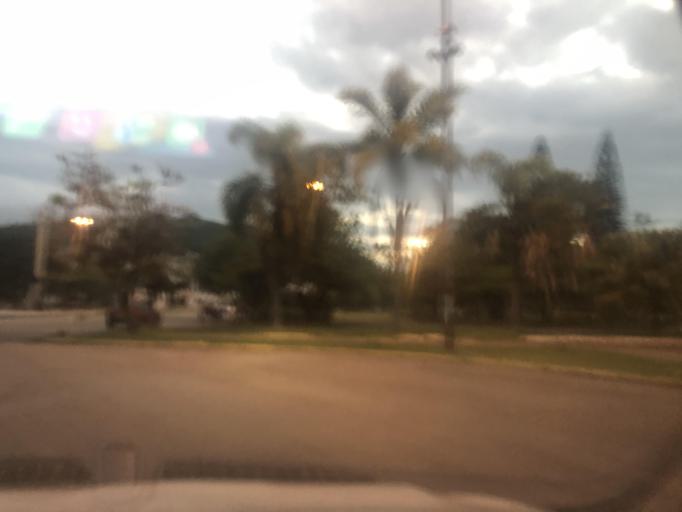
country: BR
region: Santa Catarina
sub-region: Florianopolis
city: Carvoeira
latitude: -27.6003
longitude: -48.5208
